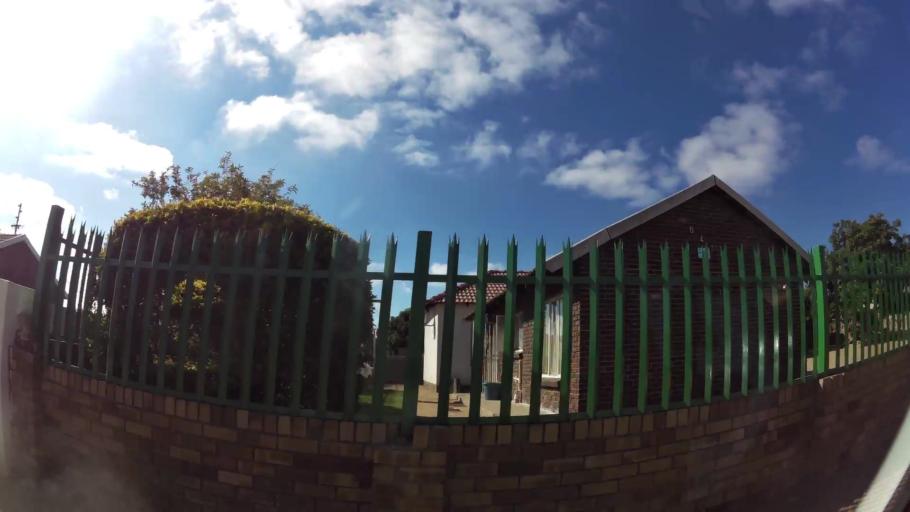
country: ZA
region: Limpopo
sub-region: Capricorn District Municipality
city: Polokwane
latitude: -23.8555
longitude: 29.3696
